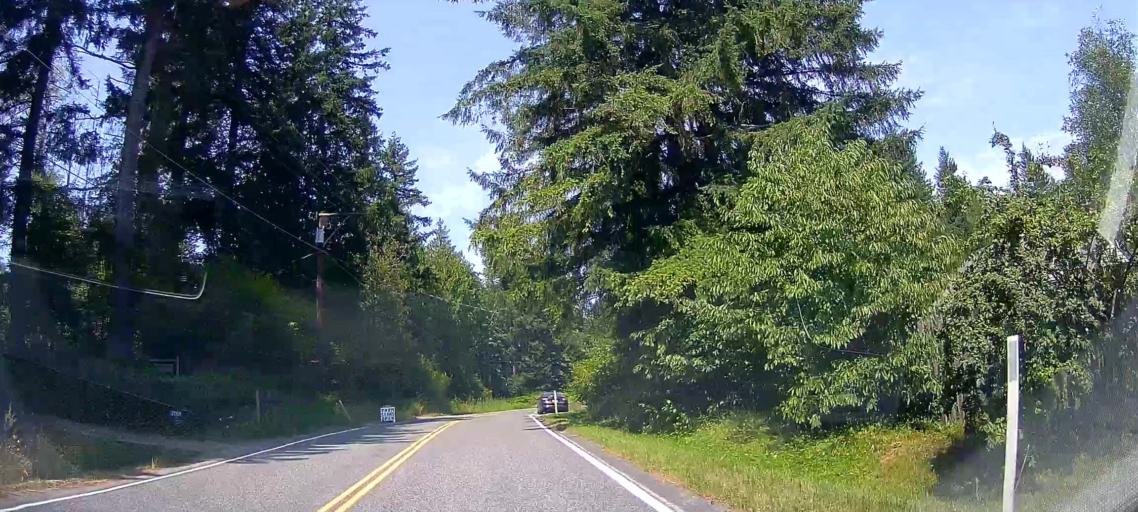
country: US
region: Washington
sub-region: Snohomish County
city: Bryant
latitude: 48.3289
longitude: -122.1390
